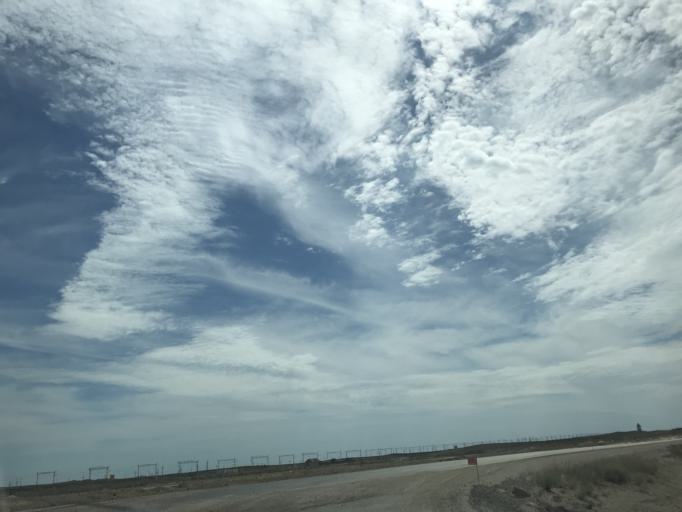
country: KZ
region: Almaty Oblysy
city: Ulken
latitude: 45.2401
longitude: 73.8280
